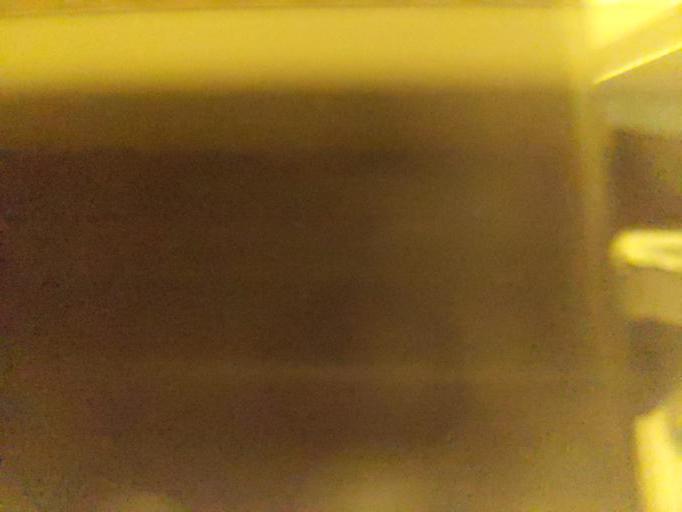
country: JP
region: Shizuoka
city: Fujinomiya
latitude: 35.1232
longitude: 138.5845
